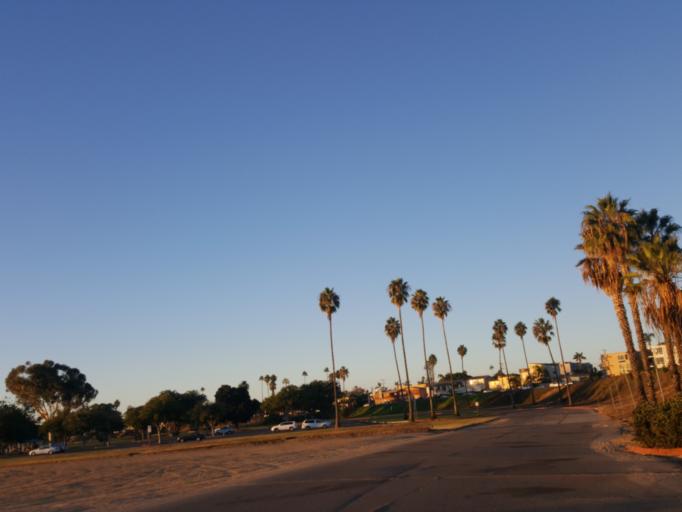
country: US
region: California
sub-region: San Diego County
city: La Jolla
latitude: 32.7898
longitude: -117.2328
